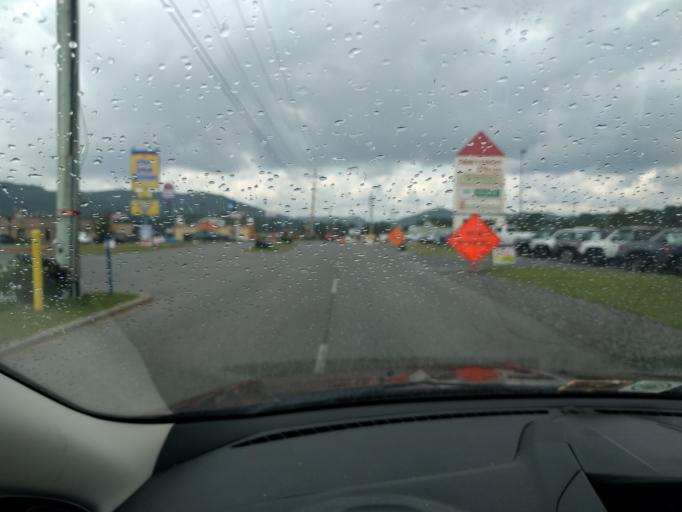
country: US
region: West Virginia
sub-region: Nicholas County
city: Summersville
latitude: 38.3048
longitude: -80.8320
